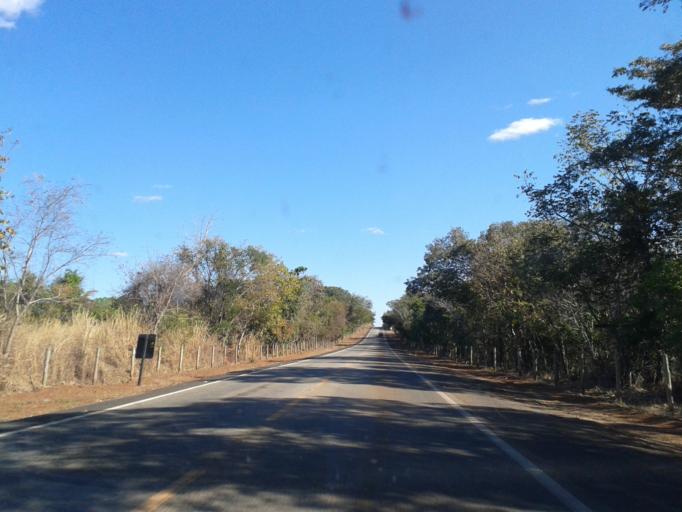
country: BR
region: Goias
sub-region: Mozarlandia
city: Mozarlandia
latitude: -14.6721
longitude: -50.5350
